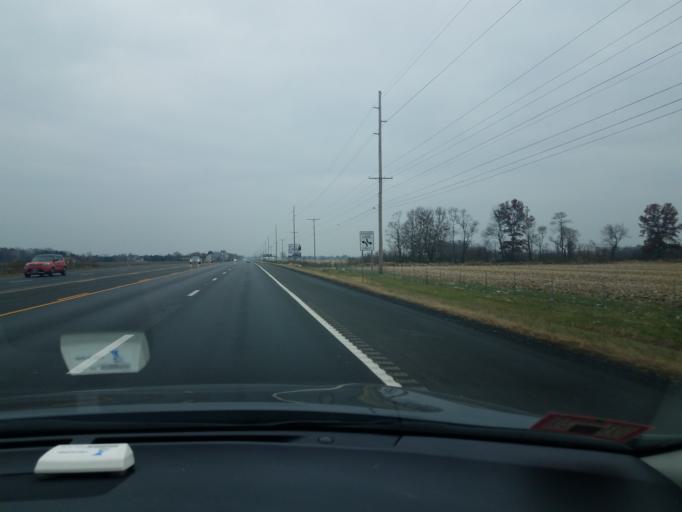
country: US
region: Ohio
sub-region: Erie County
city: Milan
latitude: 41.3644
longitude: -82.6383
